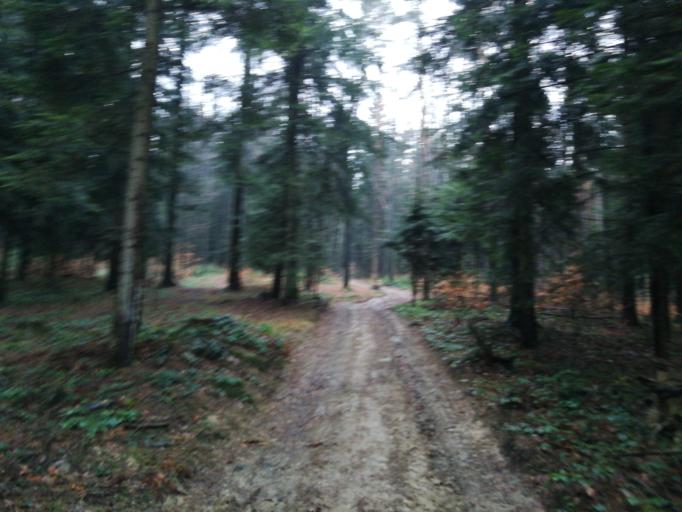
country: PL
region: Lesser Poland Voivodeship
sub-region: Powiat myslenicki
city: Osieczany
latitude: 49.8182
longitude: 19.9765
